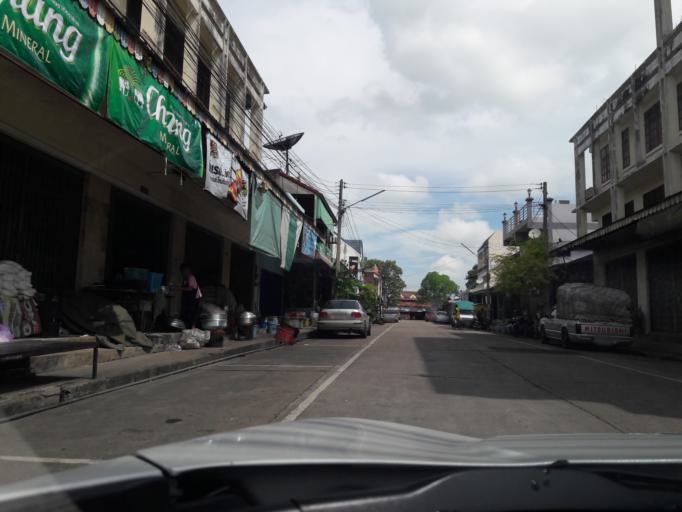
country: TH
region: Lop Buri
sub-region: Amphoe Tha Luang
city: Tha Luang
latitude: 15.0715
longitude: 101.1089
